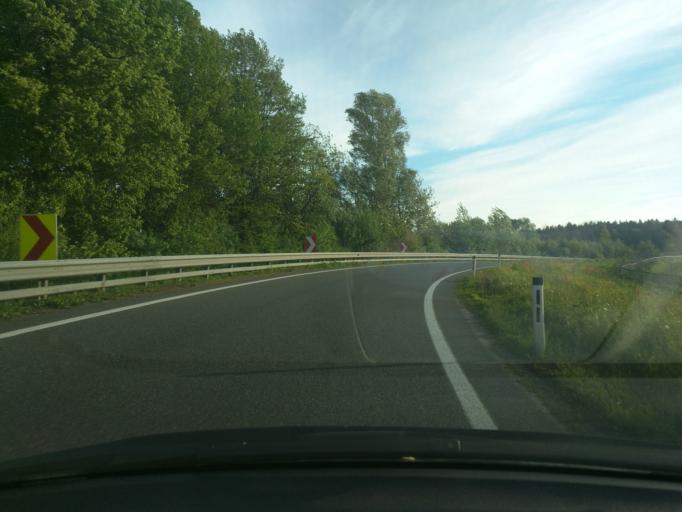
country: AT
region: Lower Austria
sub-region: Politischer Bezirk Amstetten
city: Amstetten
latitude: 48.1353
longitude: 14.8376
